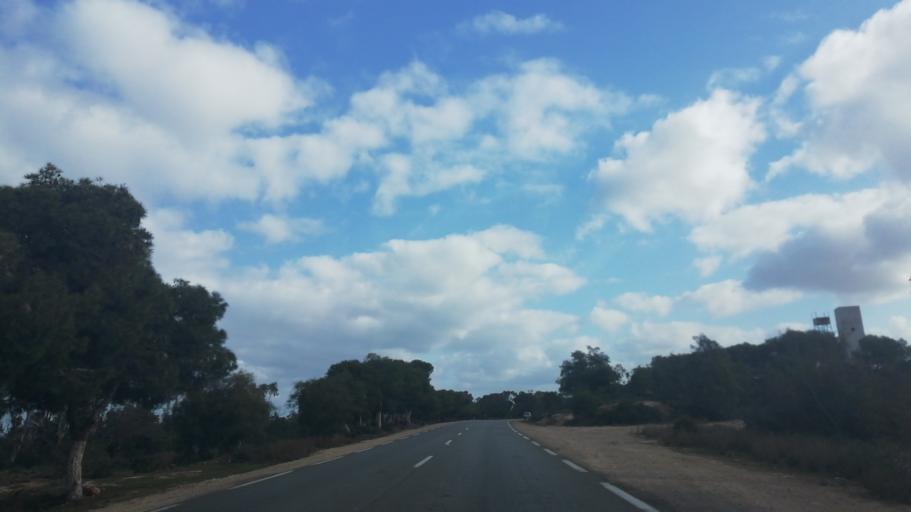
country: DZ
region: Relizane
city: Mazouna
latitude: 36.2366
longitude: 0.5244
